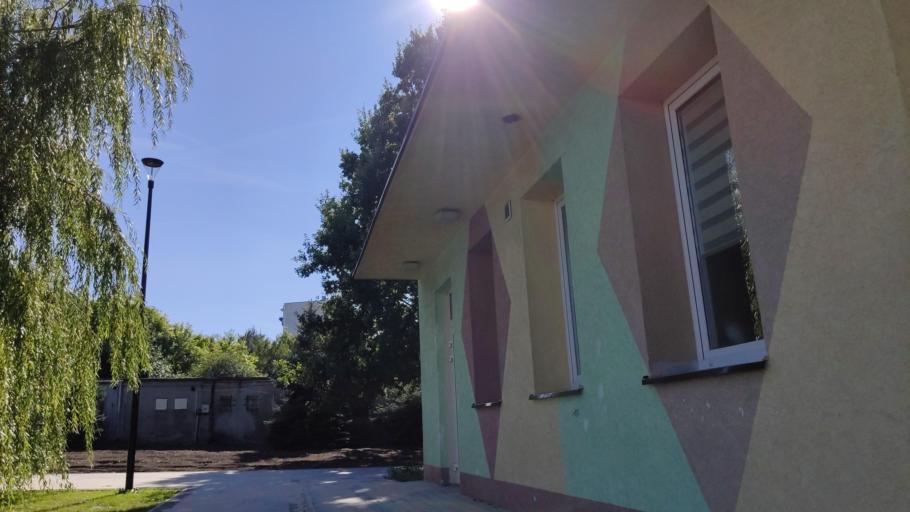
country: PL
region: Kujawsko-Pomorskie
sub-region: Powiat zninski
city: Barcin
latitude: 52.8556
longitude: 17.9409
